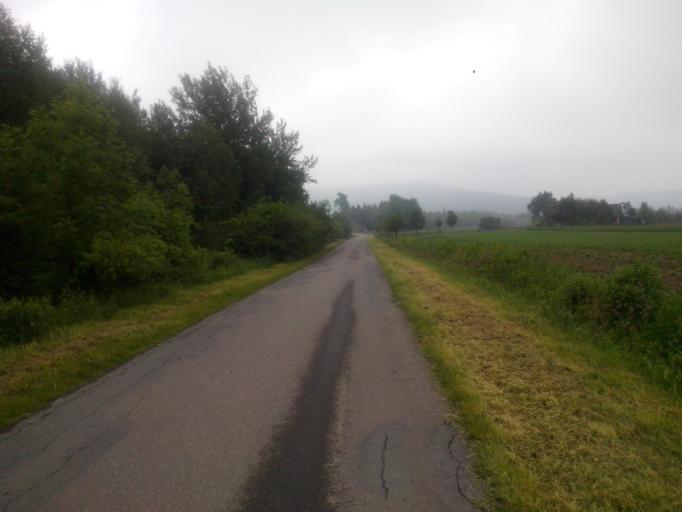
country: PL
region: Subcarpathian Voivodeship
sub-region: Powiat strzyzowski
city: Wysoka Strzyzowska
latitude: 49.8096
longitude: 21.7821
